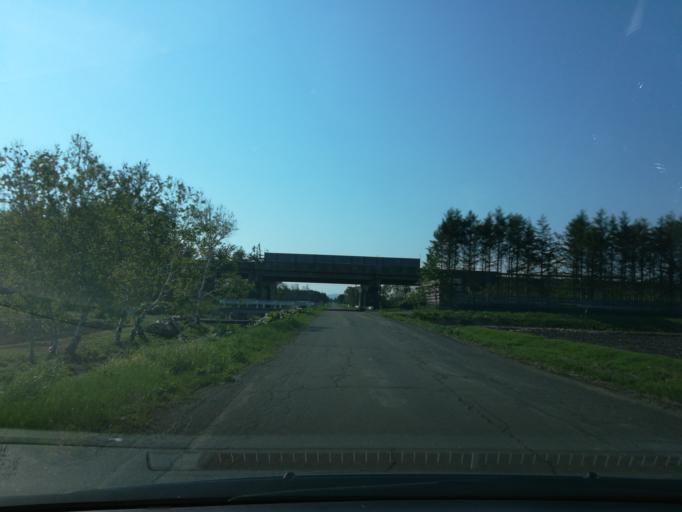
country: JP
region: Hokkaido
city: Ebetsu
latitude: 43.1201
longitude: 141.6270
